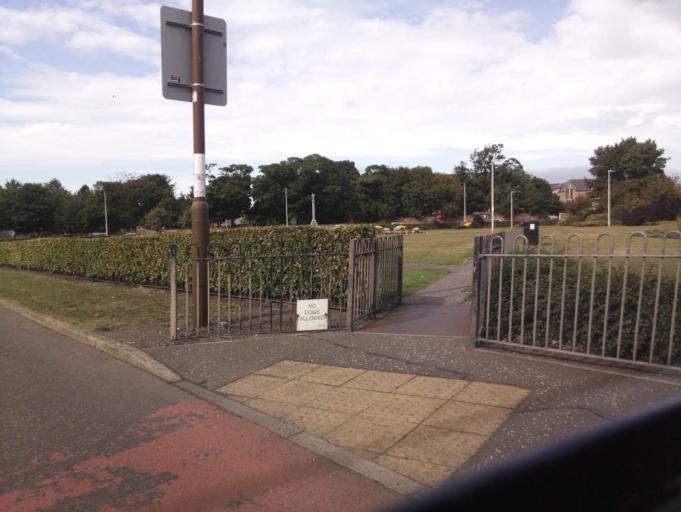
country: GB
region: Scotland
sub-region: East Lothian
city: Cockenzie
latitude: 55.9687
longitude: -2.9615
